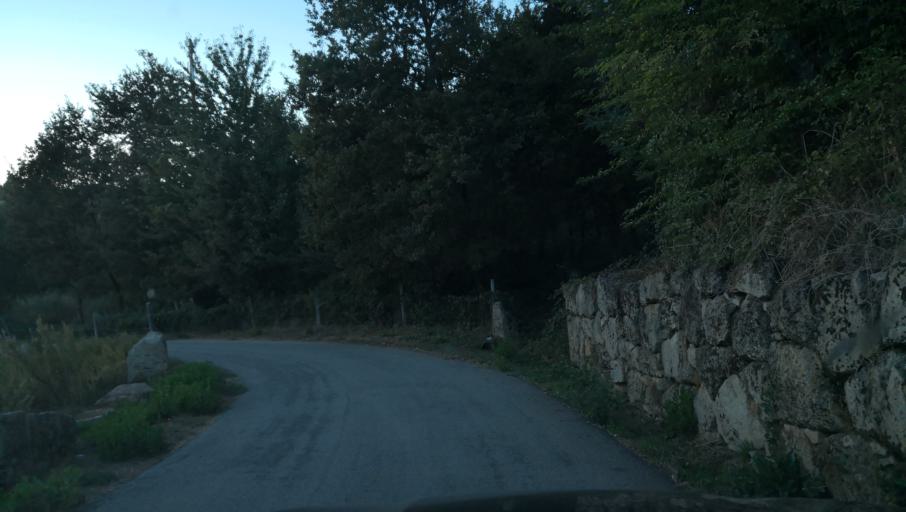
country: PT
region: Vila Real
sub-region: Vila Real
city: Vila Real
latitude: 41.3089
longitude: -7.7622
